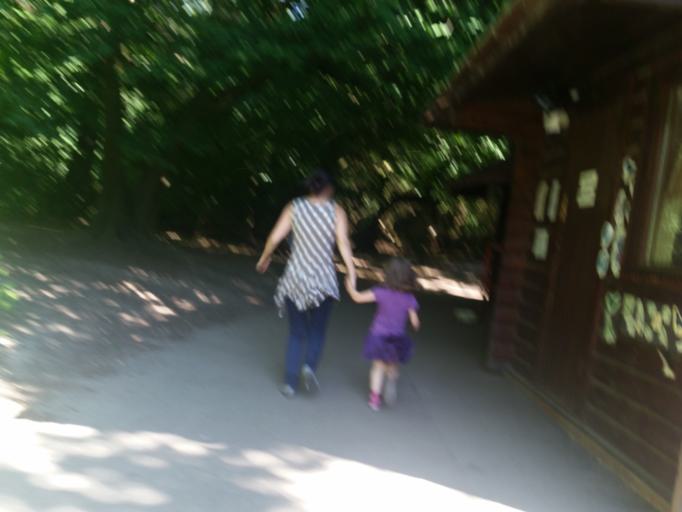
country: GB
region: England
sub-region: Greater London
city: Crouch End
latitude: 51.5798
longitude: -0.1500
